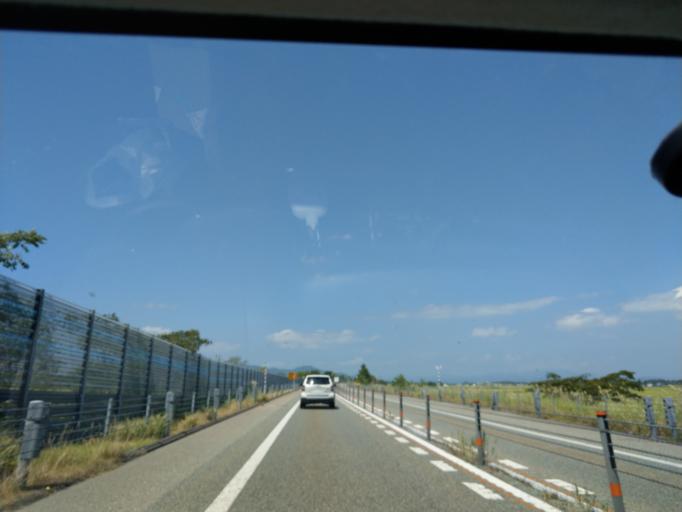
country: JP
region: Akita
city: Omagari
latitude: 39.3783
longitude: 140.4813
